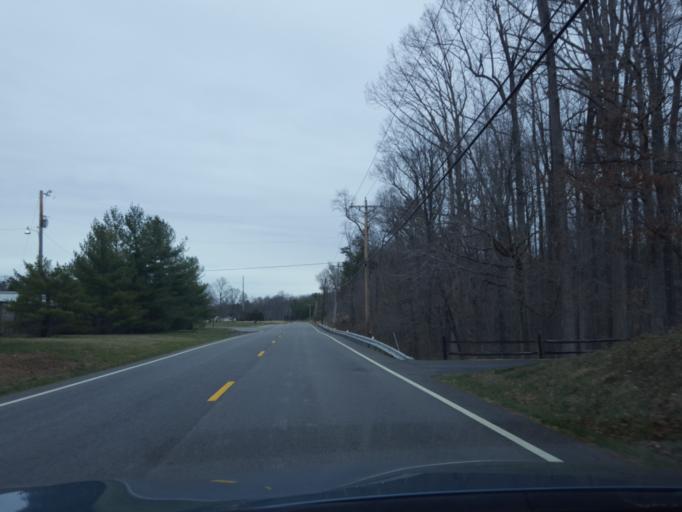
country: US
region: Maryland
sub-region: Calvert County
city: Prince Frederick
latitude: 38.5038
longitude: -76.5714
